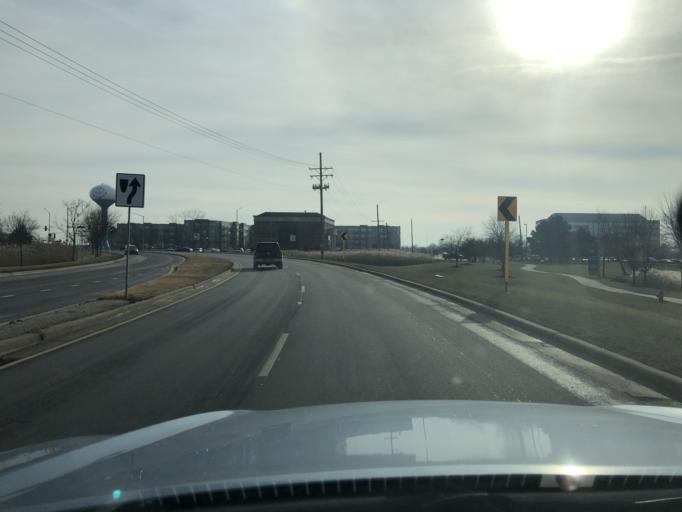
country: US
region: Illinois
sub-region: DuPage County
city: Itasca
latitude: 41.9895
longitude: -88.0033
